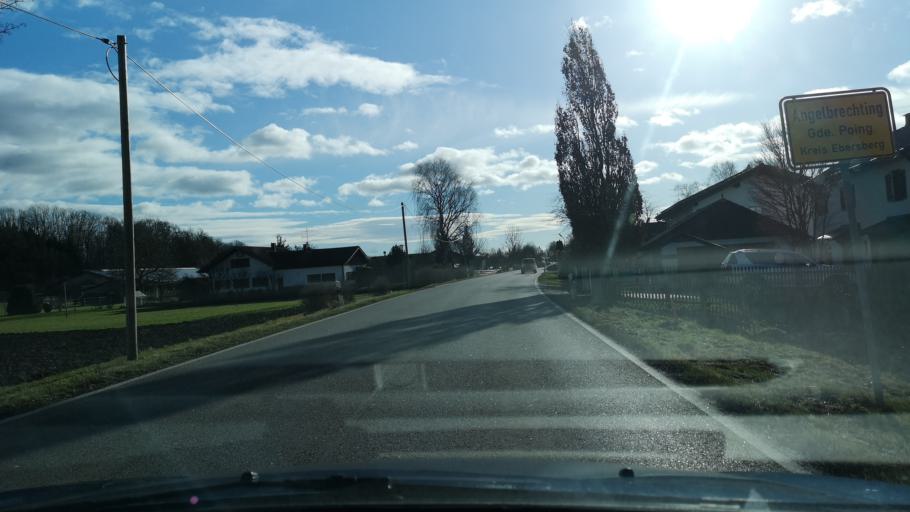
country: DE
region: Bavaria
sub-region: Upper Bavaria
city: Poing
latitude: 48.1595
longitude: 11.8163
